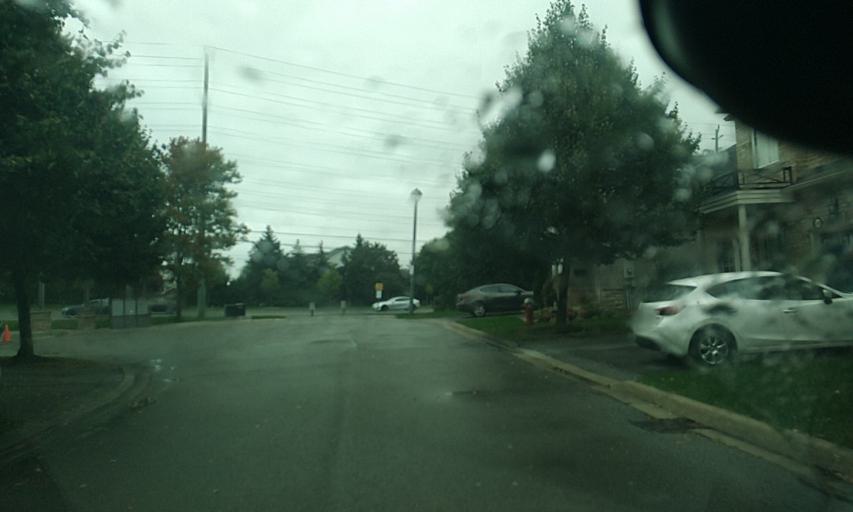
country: CA
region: Ontario
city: Newmarket
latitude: 44.0430
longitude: -79.4448
